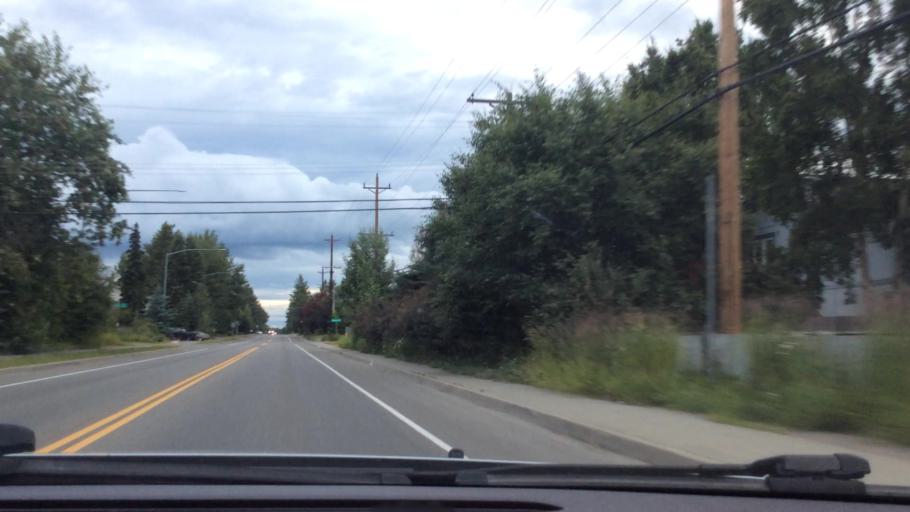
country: US
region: Alaska
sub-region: Anchorage Municipality
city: Elmendorf Air Force Base
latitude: 61.2141
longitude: -149.7559
